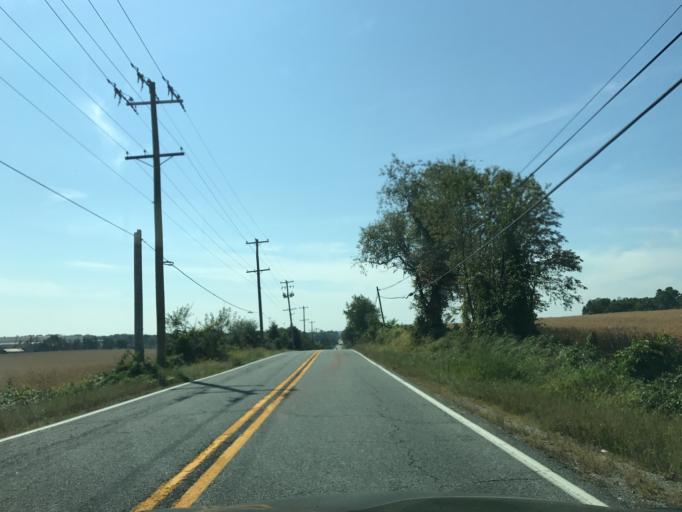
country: US
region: Maryland
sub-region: Cecil County
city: Perryville
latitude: 39.5690
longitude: -76.0524
